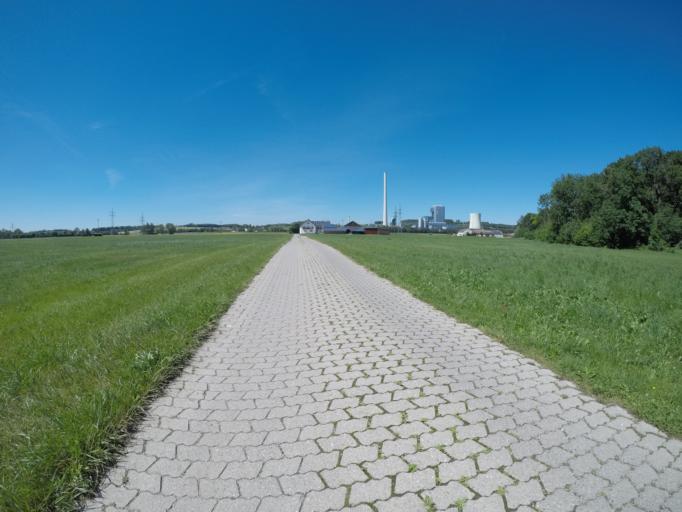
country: DE
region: Bavaria
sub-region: Upper Bavaria
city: Zolling
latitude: 48.4460
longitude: 11.7983
